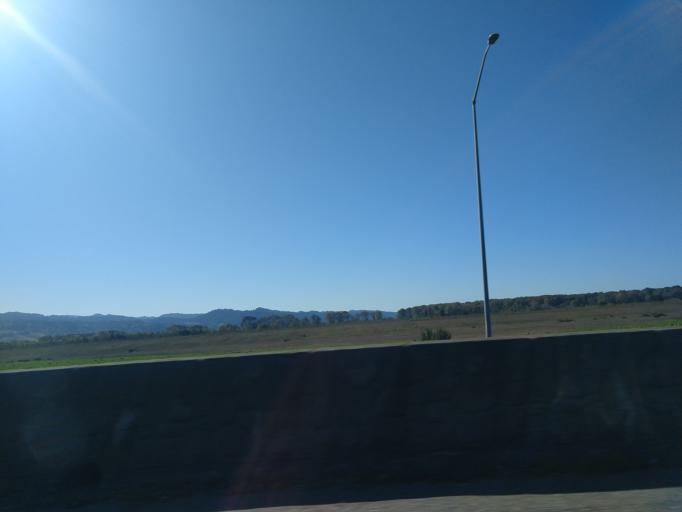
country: US
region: California
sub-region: Humboldt County
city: Fortuna
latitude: 40.5717
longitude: -124.1488
